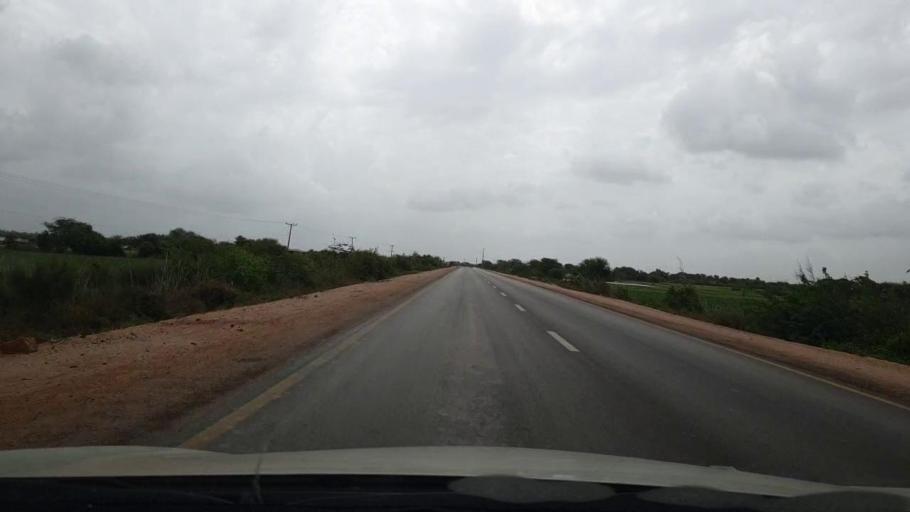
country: PK
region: Sindh
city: Mirpur Batoro
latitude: 24.6239
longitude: 68.3297
